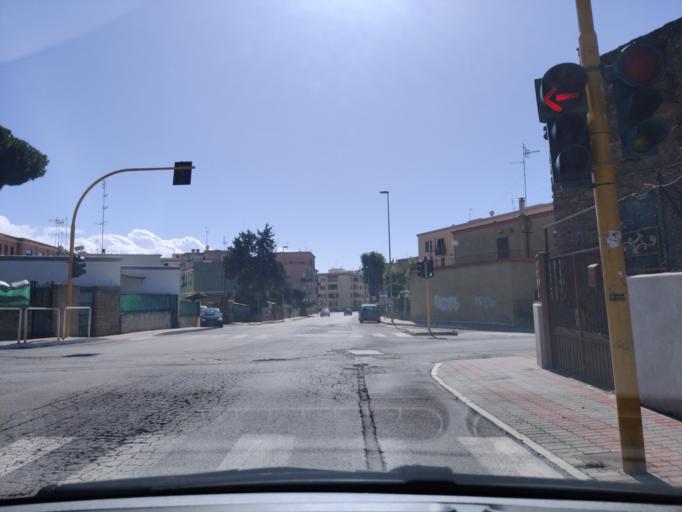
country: IT
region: Latium
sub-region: Citta metropolitana di Roma Capitale
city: Civitavecchia
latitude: 42.0904
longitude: 11.8073
